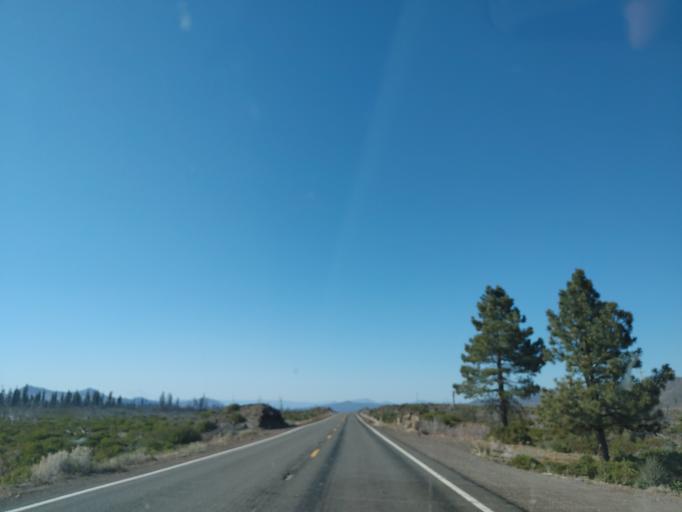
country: US
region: California
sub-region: Shasta County
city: Burney
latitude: 40.7081
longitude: -121.4198
